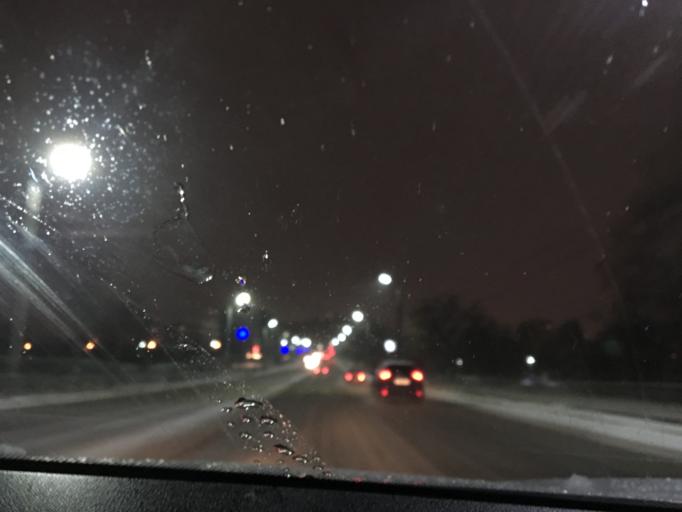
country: RU
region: Tula
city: Tula
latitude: 54.1868
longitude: 37.5769
